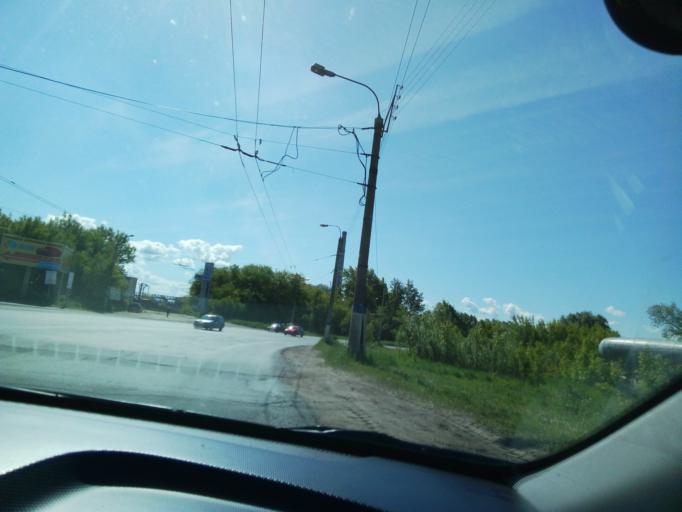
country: RU
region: Chuvashia
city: Novocheboksarsk
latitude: 56.0912
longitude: 47.5010
